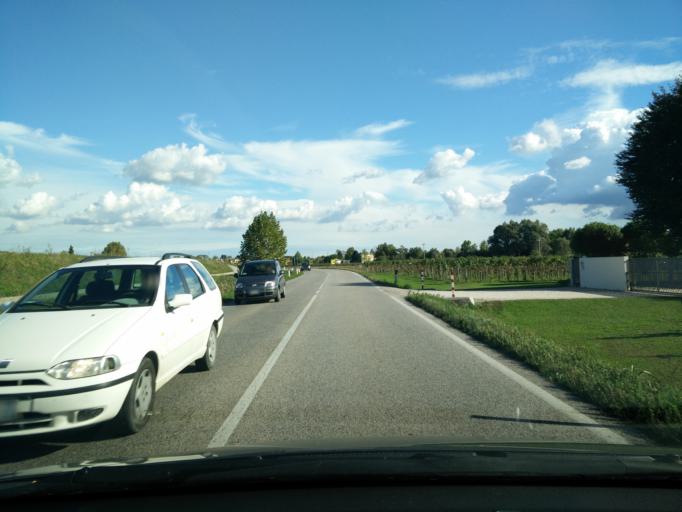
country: IT
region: Veneto
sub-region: Provincia di Treviso
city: Candelu
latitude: 45.7401
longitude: 12.3596
